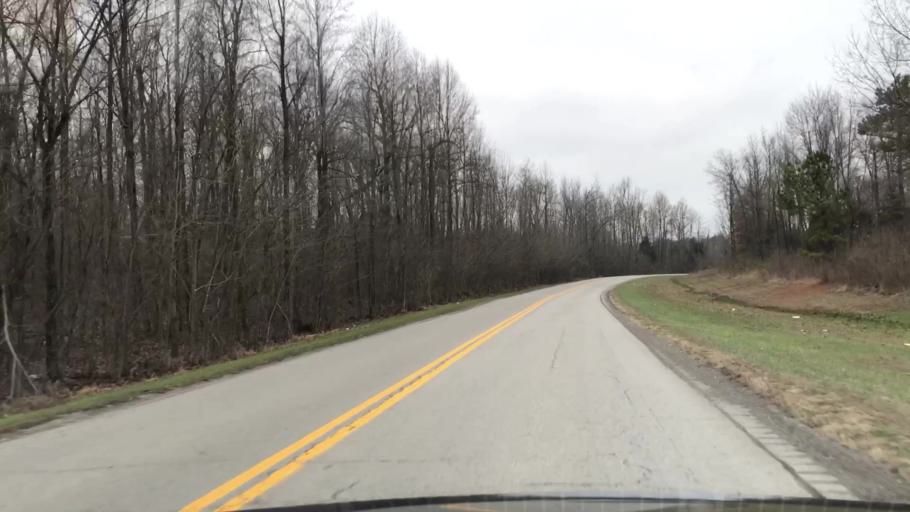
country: US
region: Kentucky
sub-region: Muhlenberg County
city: Morehead
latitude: 37.2593
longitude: -87.2061
